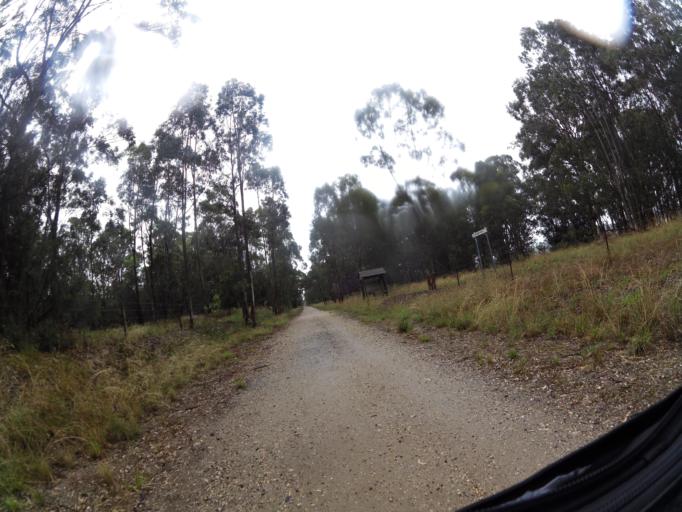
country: AU
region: Victoria
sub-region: East Gippsland
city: Lakes Entrance
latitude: -37.7940
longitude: 147.8288
